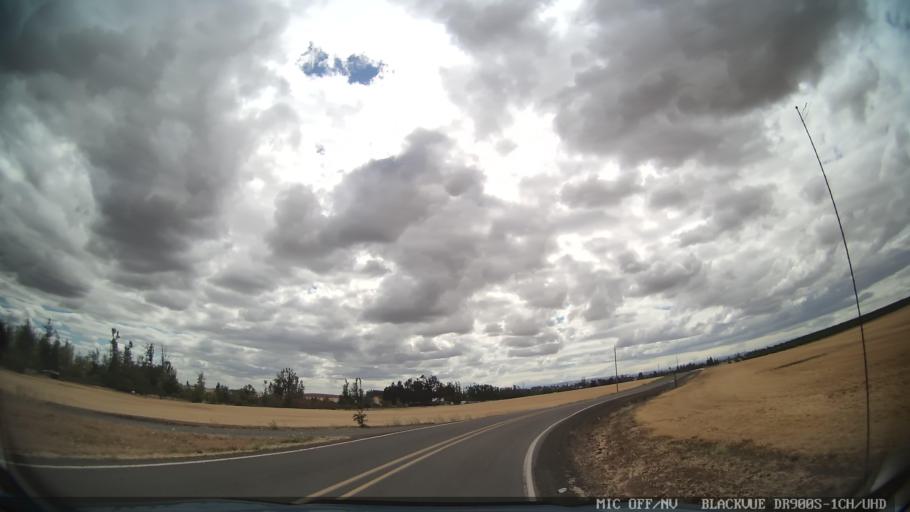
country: US
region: Oregon
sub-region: Marion County
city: Sublimity
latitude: 44.8444
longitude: -122.7541
